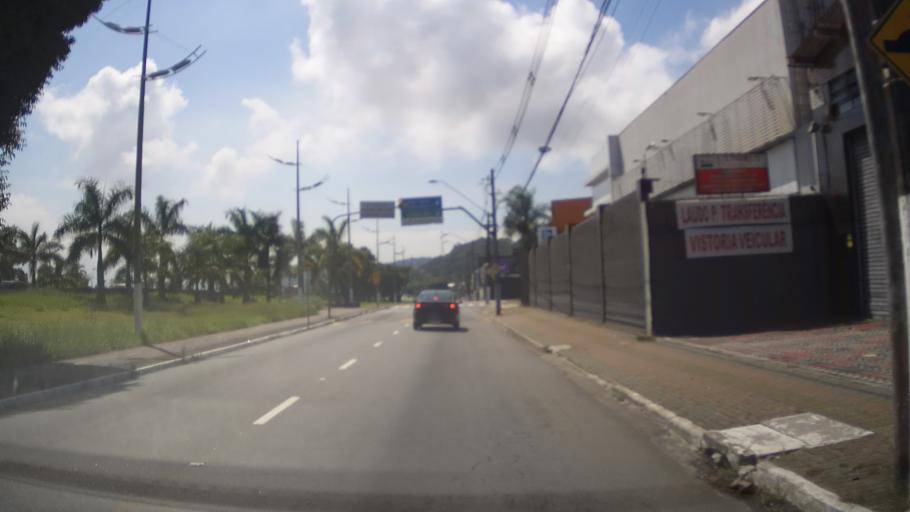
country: BR
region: Sao Paulo
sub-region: Praia Grande
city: Praia Grande
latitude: -24.0027
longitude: -46.4209
